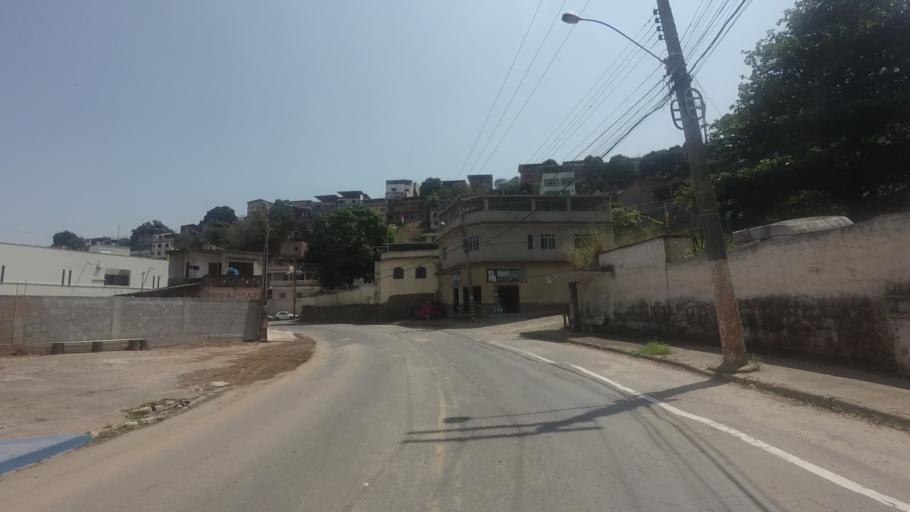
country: BR
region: Espirito Santo
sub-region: Cachoeiro De Itapemirim
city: Cachoeiro de Itapemirim
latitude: -20.8517
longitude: -41.0934
